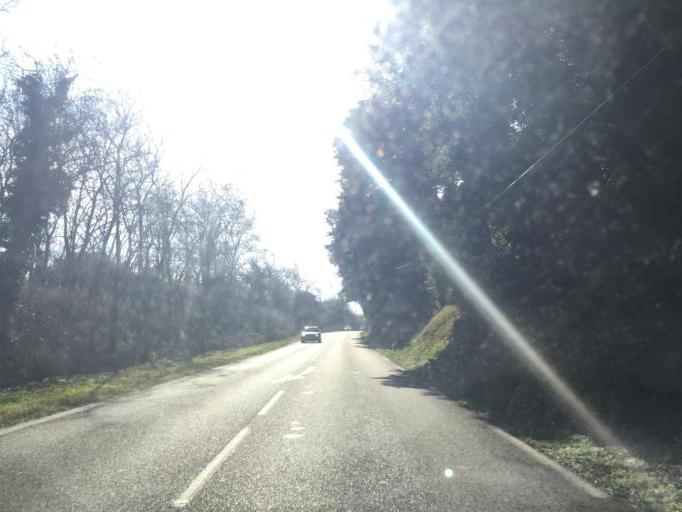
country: FR
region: Languedoc-Roussillon
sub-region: Departement du Gard
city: Sauveterre
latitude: 44.0019
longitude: 4.8120
